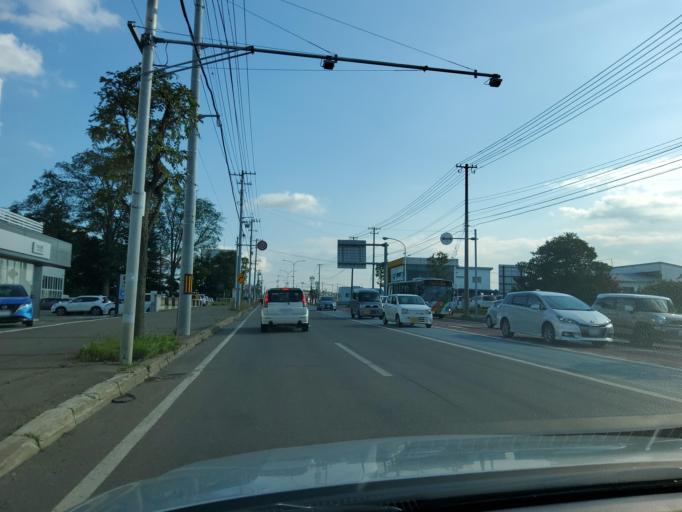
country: JP
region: Hokkaido
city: Obihiro
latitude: 42.8993
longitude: 143.2084
